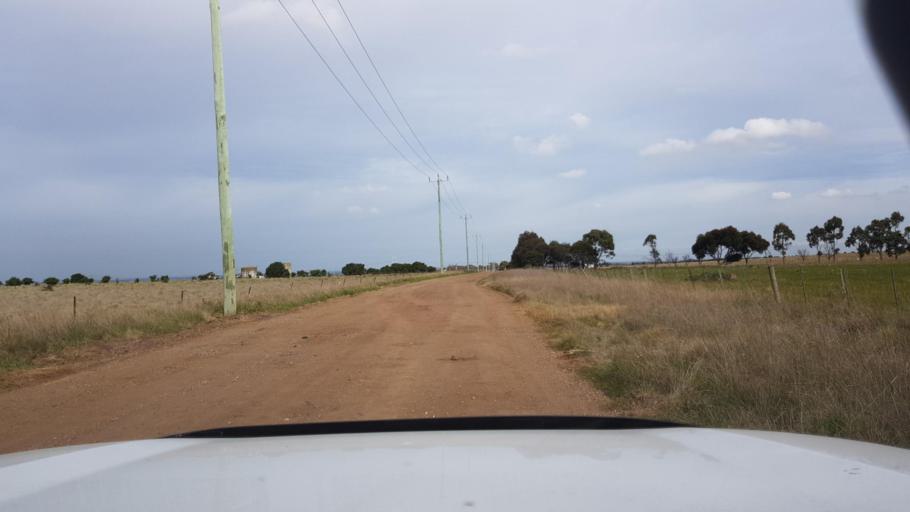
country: AU
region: Victoria
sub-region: Melton
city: Rockbank
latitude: -37.7590
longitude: 144.6471
